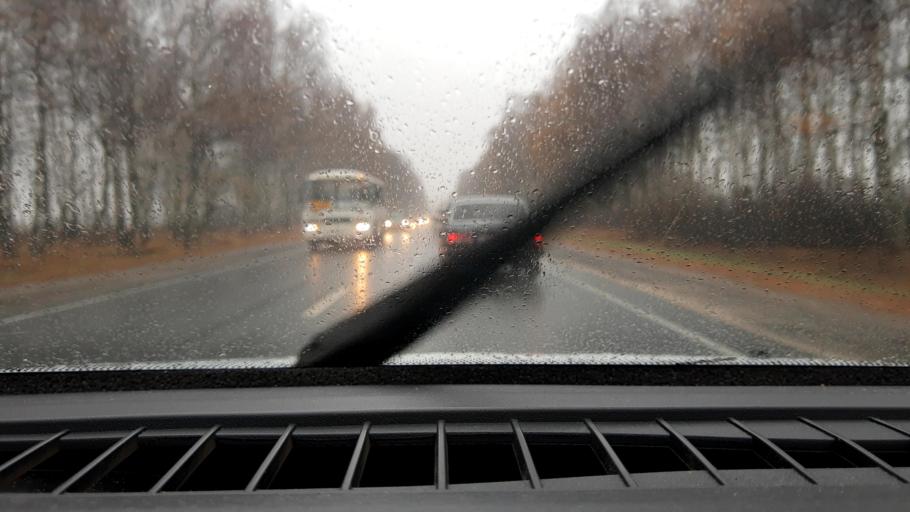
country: RU
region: Nizjnij Novgorod
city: Sitniki
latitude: 56.5168
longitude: 44.0248
